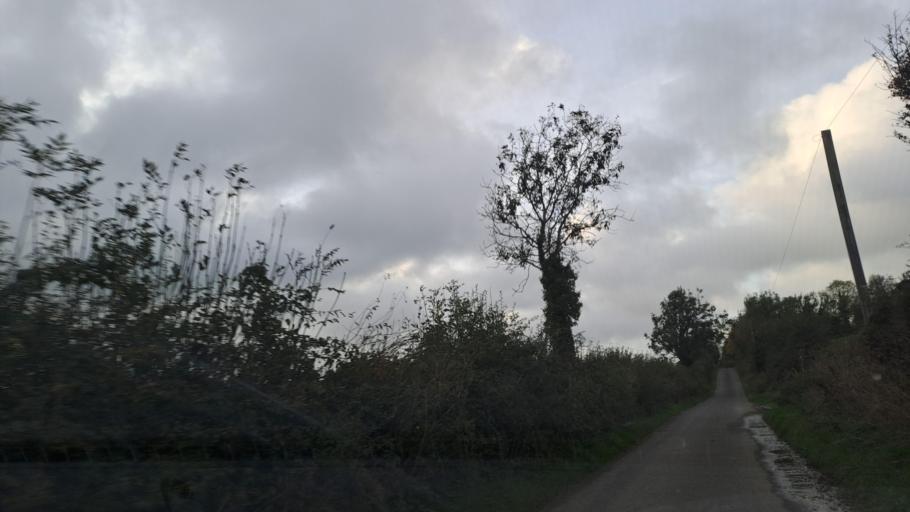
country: IE
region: Ulster
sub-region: County Monaghan
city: Carrickmacross
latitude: 54.0170
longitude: -6.7592
